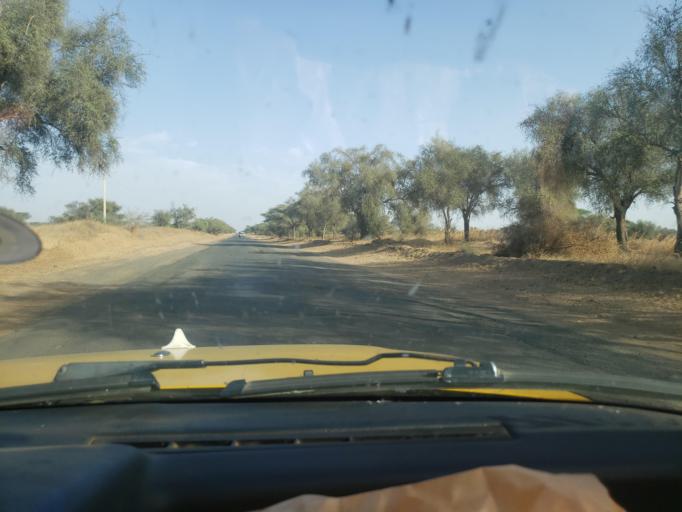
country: SN
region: Louga
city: Louga
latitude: 15.5054
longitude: -15.9594
